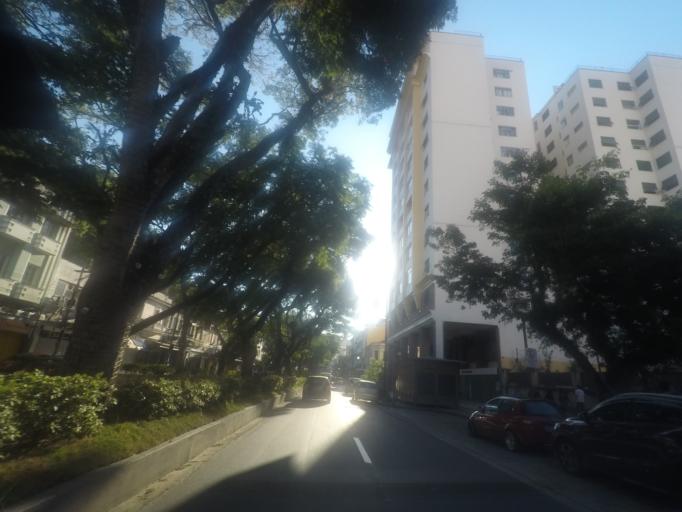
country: BR
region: Rio de Janeiro
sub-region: Petropolis
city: Petropolis
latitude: -22.5090
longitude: -43.1734
